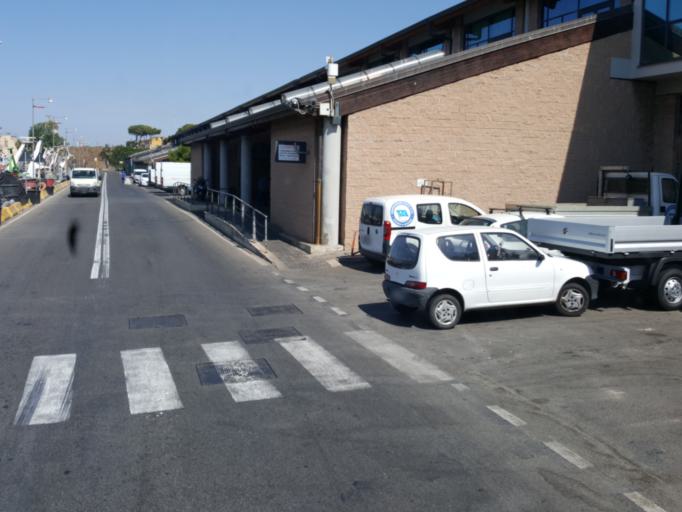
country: IT
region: Latium
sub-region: Citta metropolitana di Roma Capitale
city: Civitavecchia
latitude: 42.0944
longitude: 11.7895
